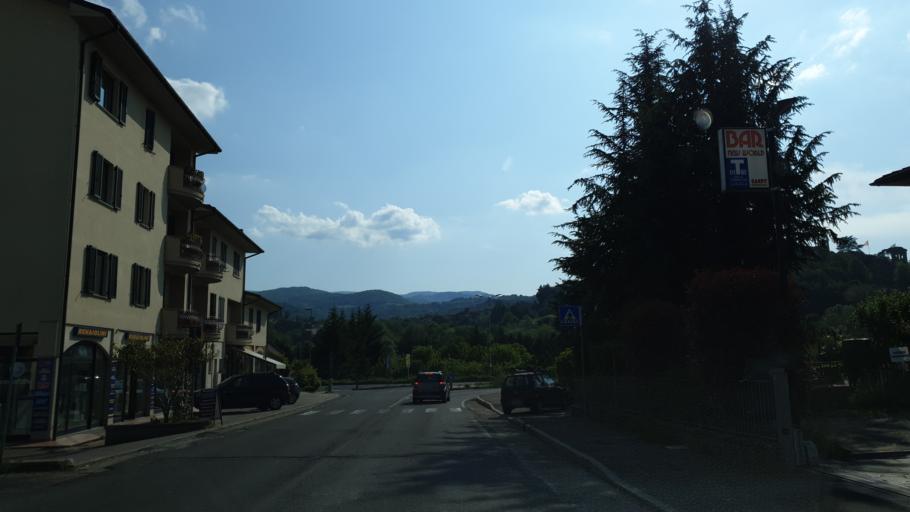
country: IT
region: Tuscany
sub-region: Province of Arezzo
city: Poppi
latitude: 43.7234
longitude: 11.7767
